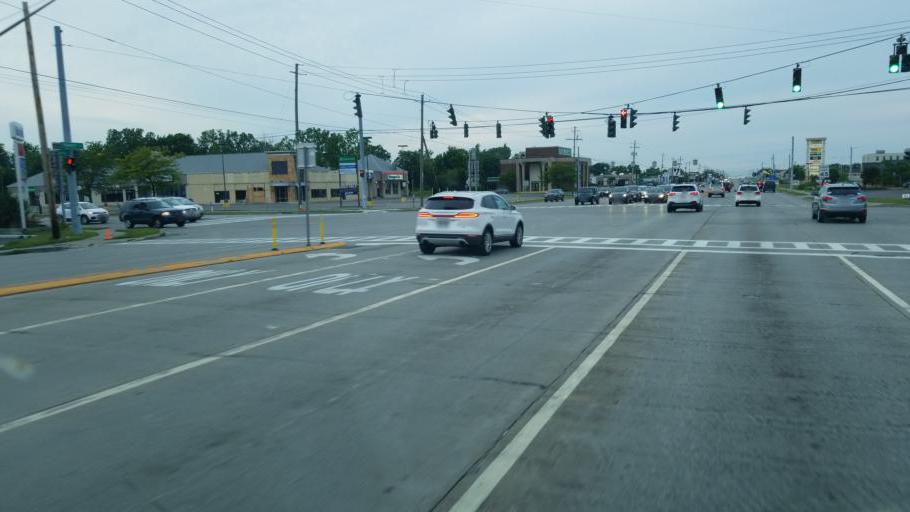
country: US
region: New York
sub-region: Erie County
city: Harris Hill
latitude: 42.9648
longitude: -78.6967
